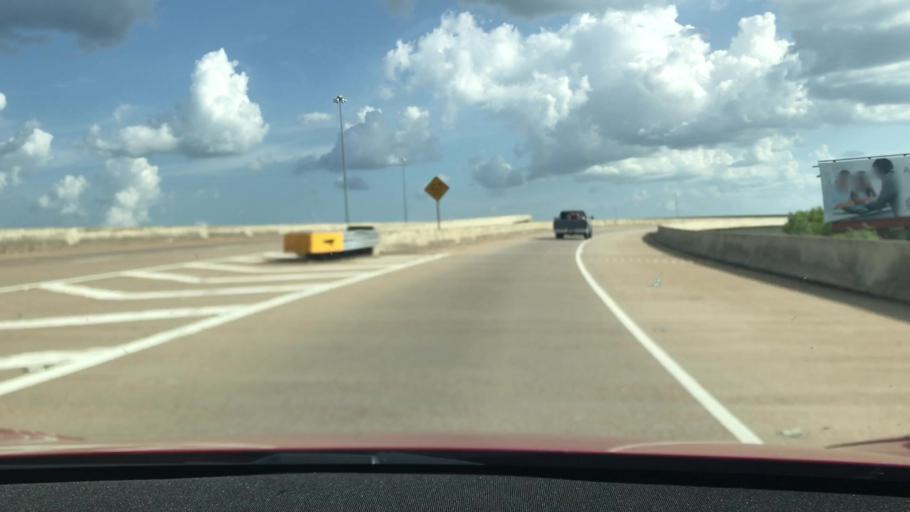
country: US
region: Louisiana
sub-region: Bossier Parish
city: Bossier City
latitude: 32.4223
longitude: -93.7500
